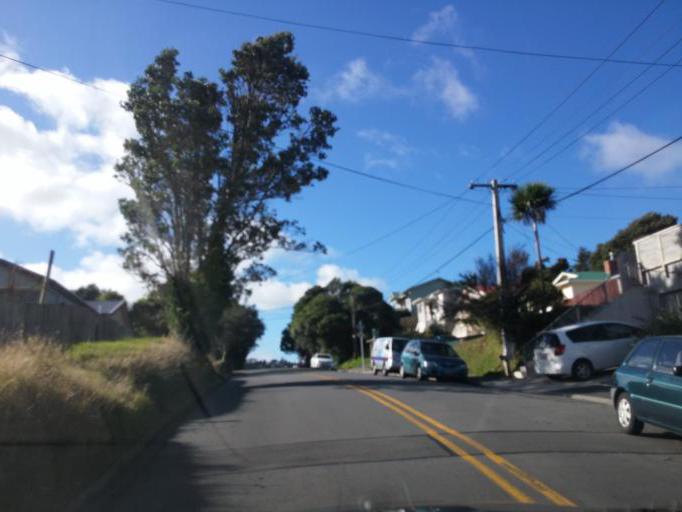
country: NZ
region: Wellington
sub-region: Wellington City
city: Kelburn
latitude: -41.2498
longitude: 174.7806
